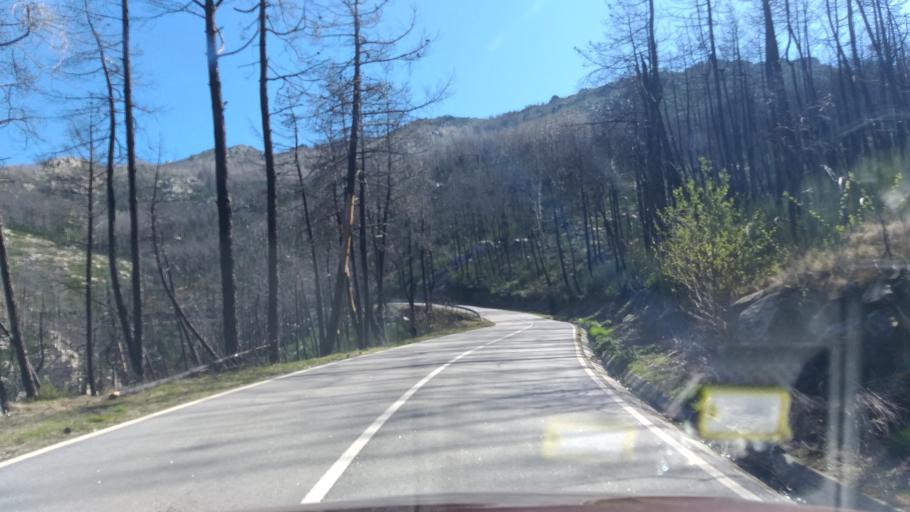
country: PT
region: Guarda
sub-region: Manteigas
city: Manteigas
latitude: 40.4895
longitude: -7.5391
